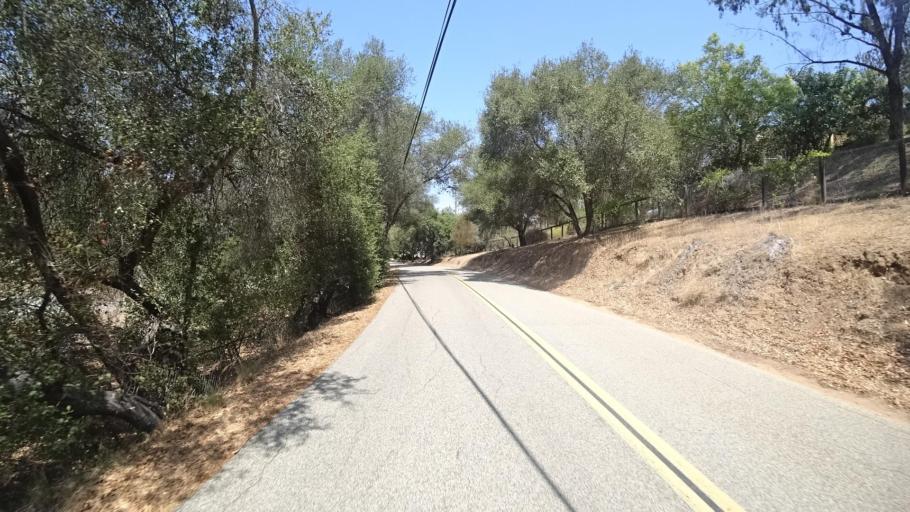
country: US
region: California
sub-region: San Diego County
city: Bonsall
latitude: 33.3250
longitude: -117.2172
